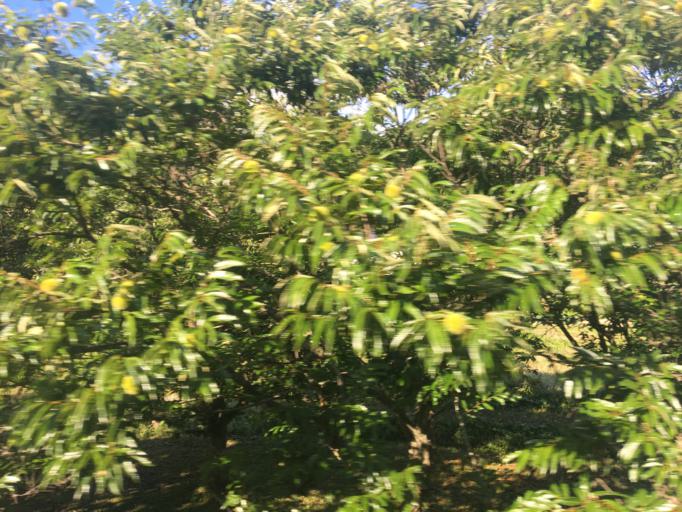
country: JP
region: Akita
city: Kakunodatemachi
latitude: 39.9203
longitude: 140.5135
